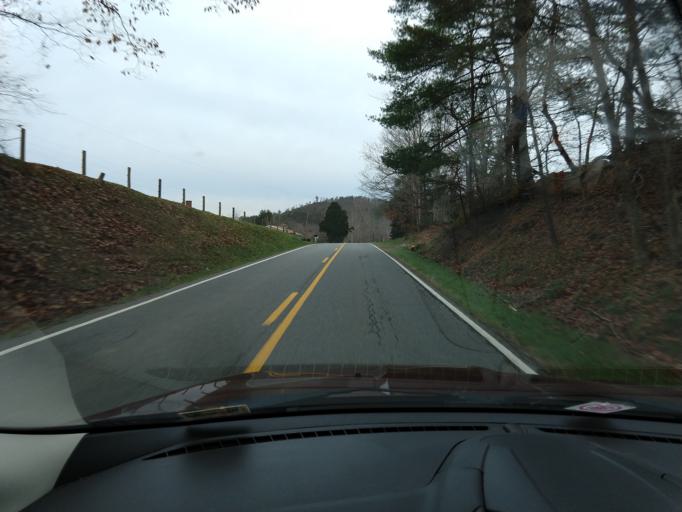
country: US
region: West Virginia
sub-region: Greenbrier County
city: White Sulphur Springs
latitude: 37.7497
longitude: -80.1667
